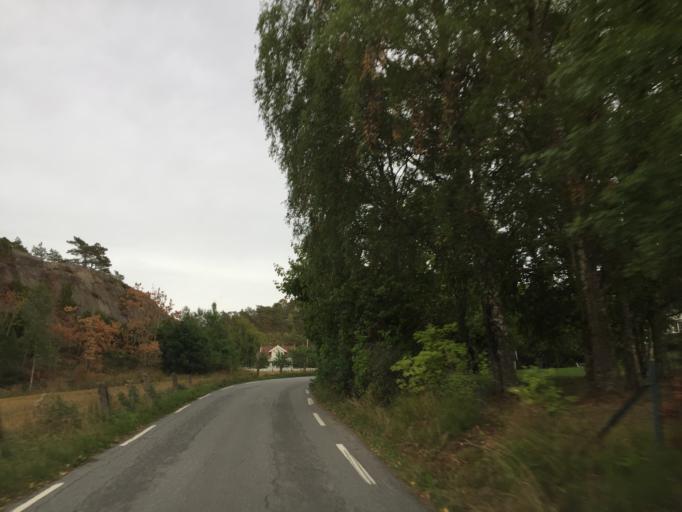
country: NO
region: Ostfold
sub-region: Hvaler
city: Skjaerhalden
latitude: 59.0576
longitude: 11.0049
